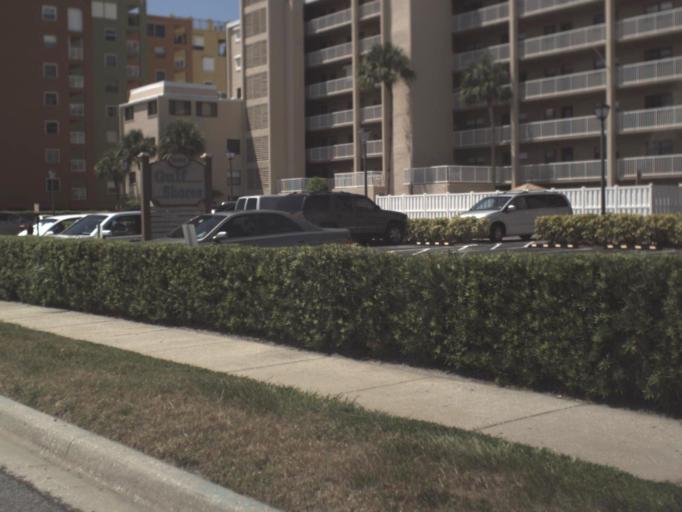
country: US
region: Florida
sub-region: Pinellas County
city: Redington Shores
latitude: 27.8407
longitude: -82.8392
